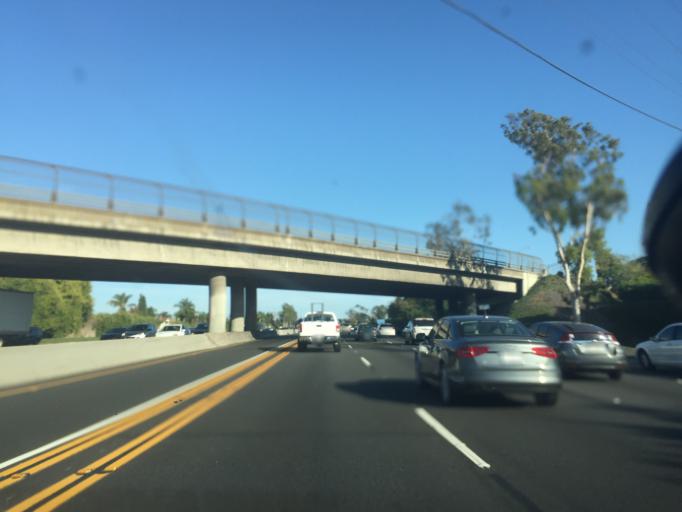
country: US
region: California
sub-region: Orange County
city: Fountain Valley
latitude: 33.7131
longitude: -117.9637
